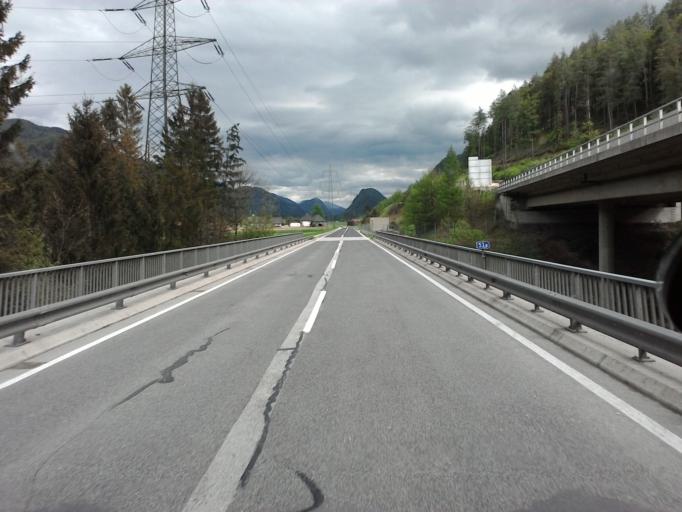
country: AT
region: Upper Austria
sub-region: Politischer Bezirk Kirchdorf an der Krems
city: Rossleithen
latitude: 47.7679
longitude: 14.1870
